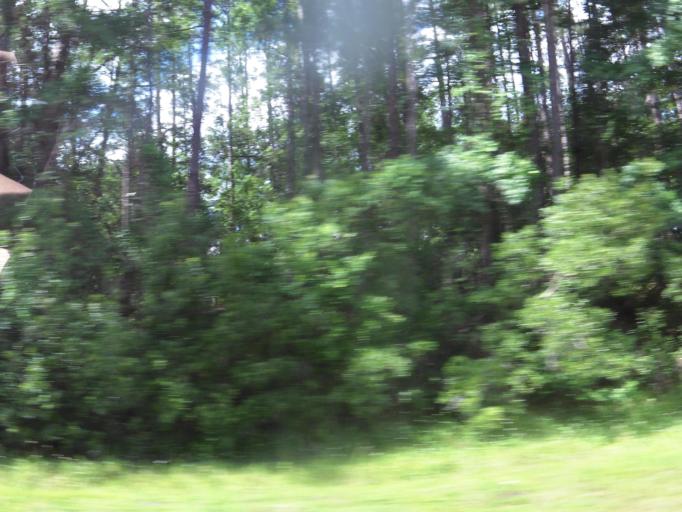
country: US
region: Florida
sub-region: Clay County
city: Asbury Lake
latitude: 29.9129
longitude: -81.8891
